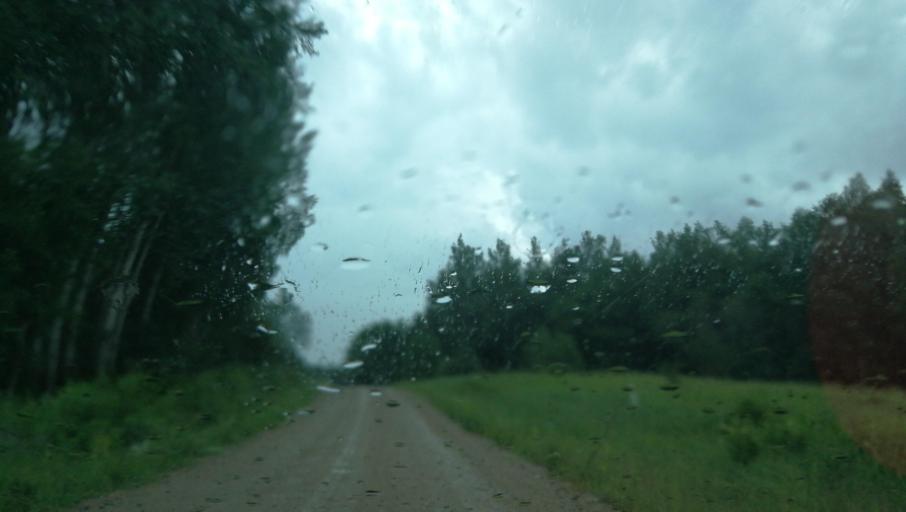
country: LV
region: Vecpiebalga
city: Vecpiebalga
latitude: 57.1052
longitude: 25.6916
